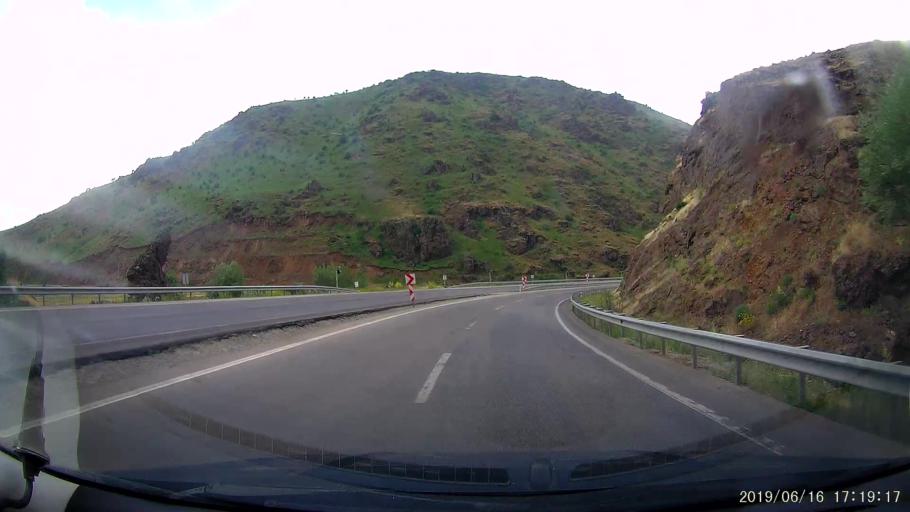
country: TR
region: Erzincan
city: Tercan
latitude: 39.8021
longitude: 40.5309
